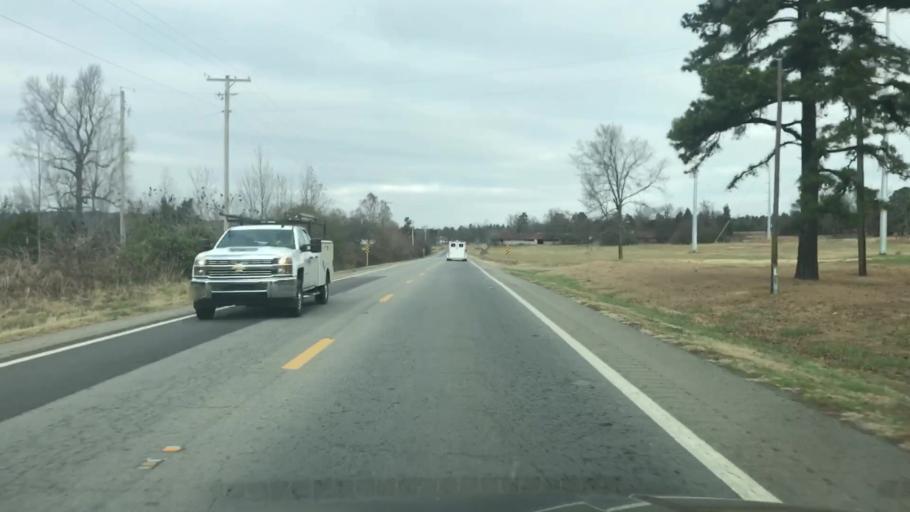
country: US
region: Arkansas
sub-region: Scott County
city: Waldron
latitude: 34.9439
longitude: -94.1033
